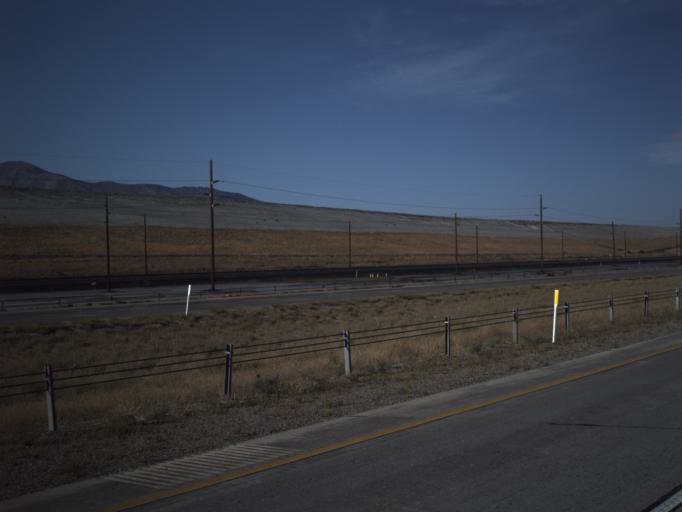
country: US
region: Utah
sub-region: Salt Lake County
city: Magna
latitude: 40.7710
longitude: -112.1286
